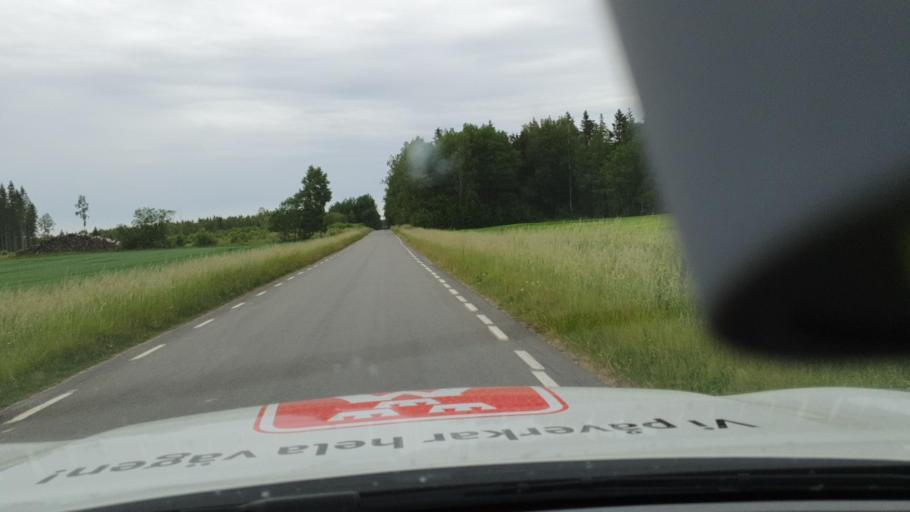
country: SE
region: Vaestra Goetaland
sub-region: Tibro Kommun
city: Tibro
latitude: 58.3366
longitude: 14.1031
